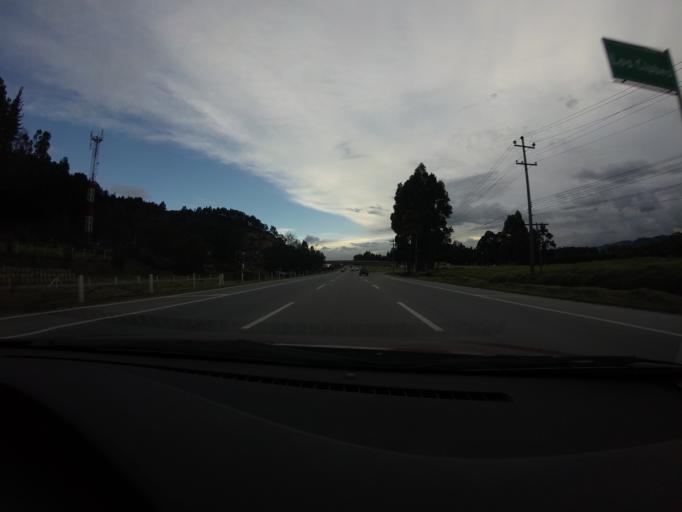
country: CO
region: Cundinamarca
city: Cajica
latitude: 4.9333
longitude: -73.9901
